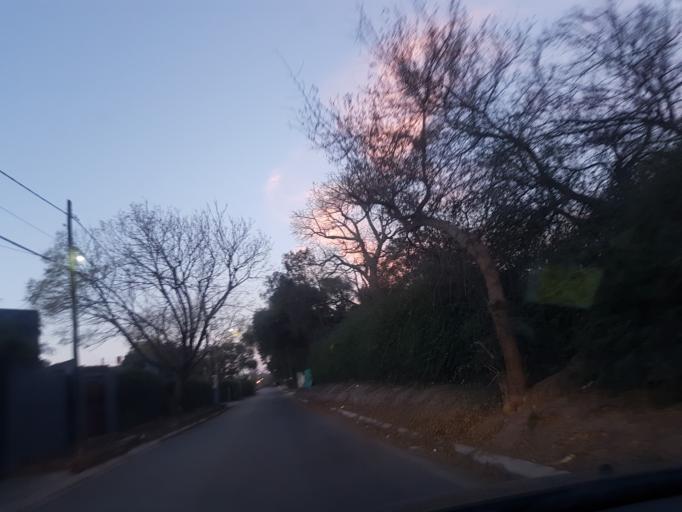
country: AR
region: Cordoba
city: Villa Allende
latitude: -31.2805
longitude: -64.2850
